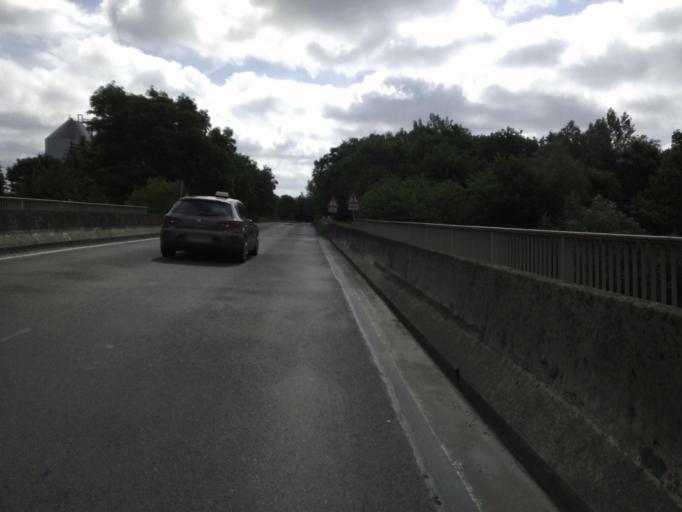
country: DE
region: Berlin
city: Blankenfelde
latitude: 52.6620
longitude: 13.4094
